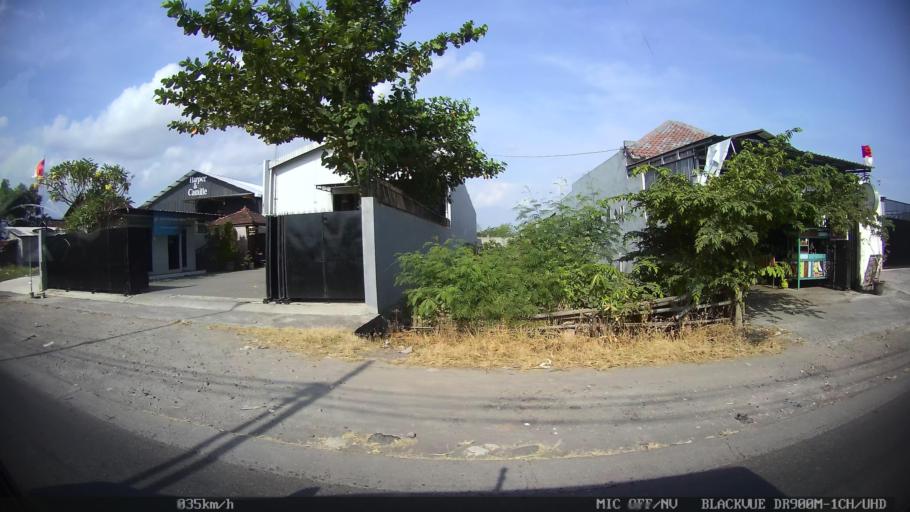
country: ID
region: Daerah Istimewa Yogyakarta
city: Kasihan
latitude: -7.8426
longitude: 110.3438
